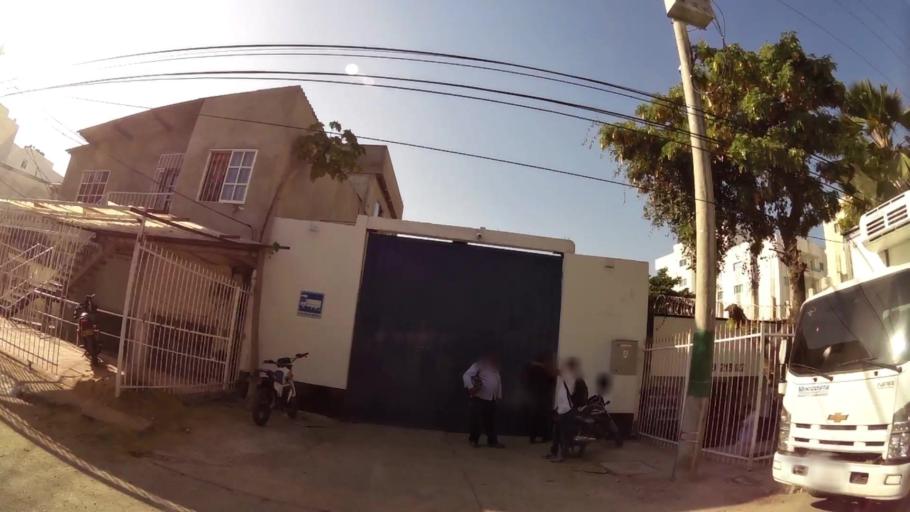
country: CO
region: Bolivar
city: Cartagena
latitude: 10.3949
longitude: -75.5184
